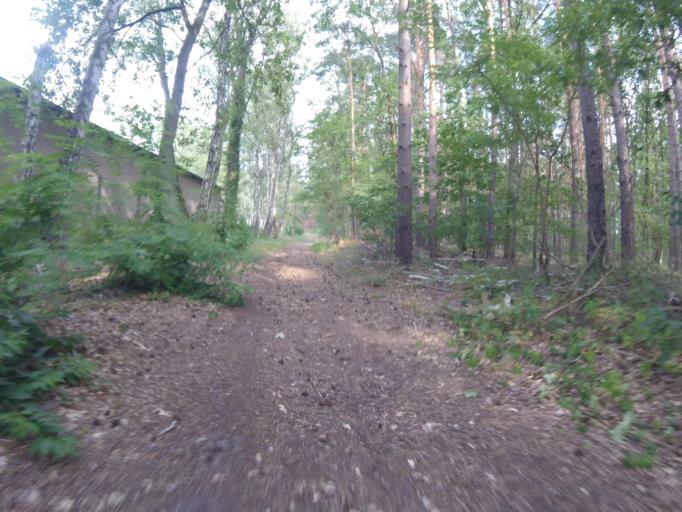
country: DE
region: Brandenburg
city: Spreenhagen
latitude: 52.2763
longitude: 13.8102
